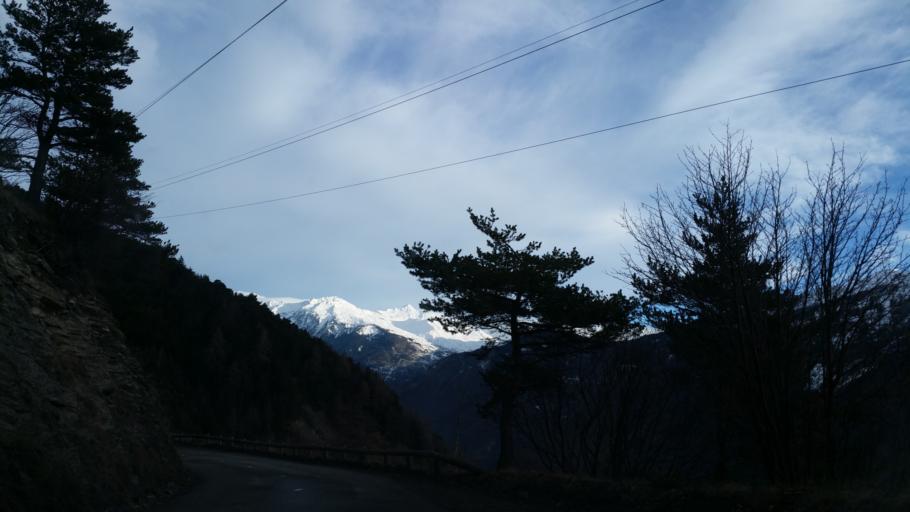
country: FR
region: Rhone-Alpes
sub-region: Departement de la Savoie
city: Villargondran
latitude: 45.2767
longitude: 6.3825
